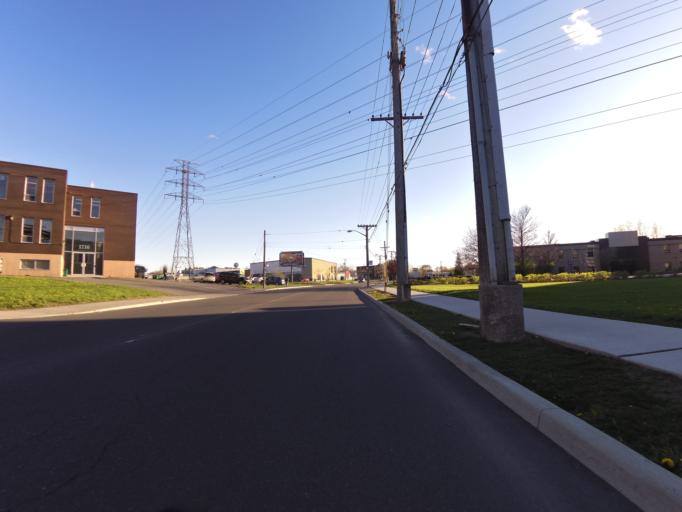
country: CA
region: Ontario
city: Ottawa
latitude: 45.3725
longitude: -75.7500
